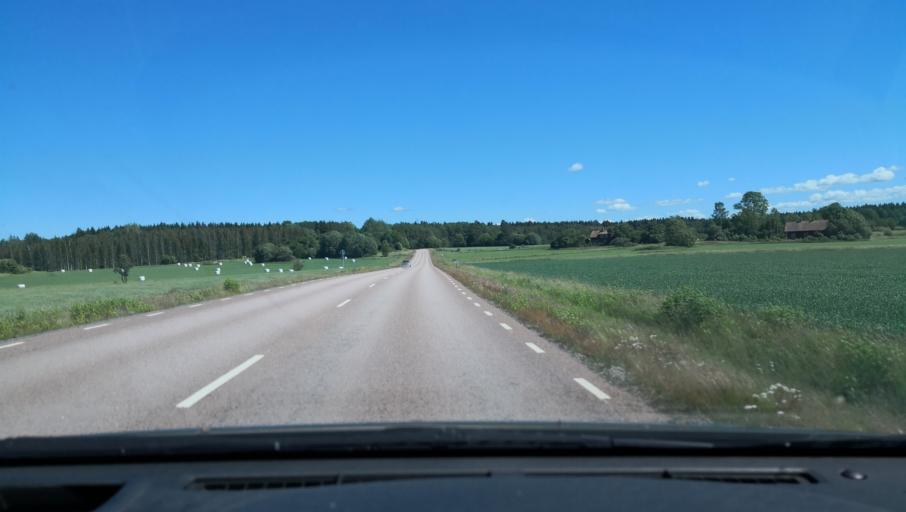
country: SE
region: Vaestmanland
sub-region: Kungsors Kommun
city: Kungsoer
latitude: 59.2895
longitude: 16.0957
